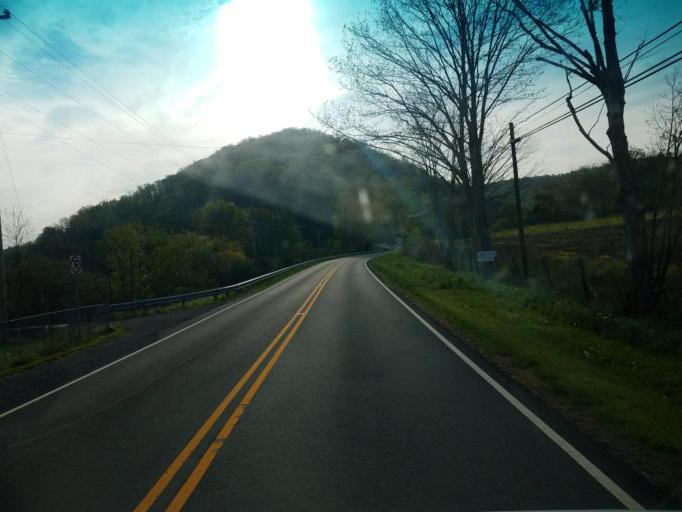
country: US
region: Virginia
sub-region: Smyth County
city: Marion
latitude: 36.8235
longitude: -81.4766
